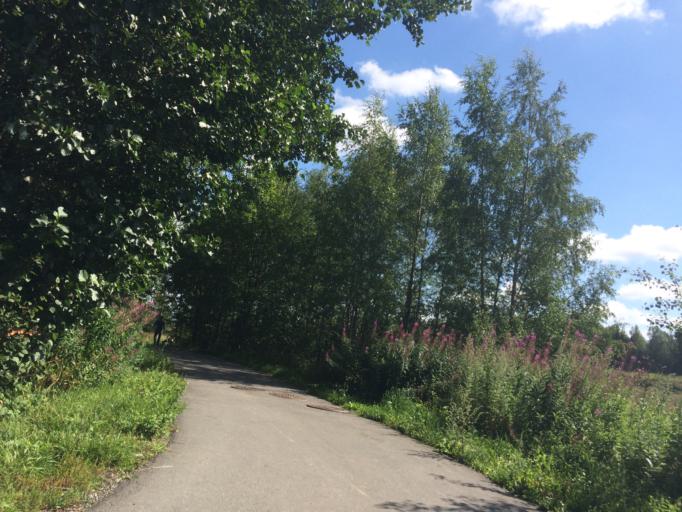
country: NO
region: Akershus
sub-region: Ski
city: Ski
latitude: 59.7142
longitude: 10.8230
